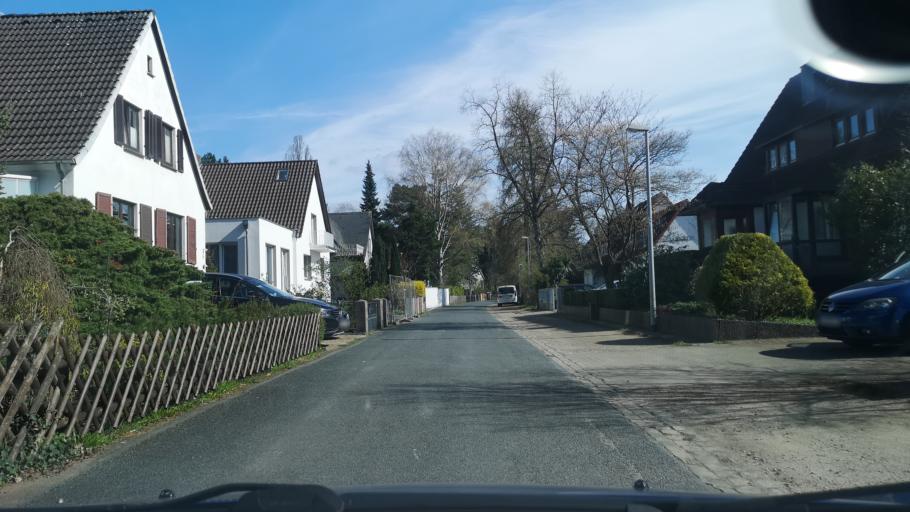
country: DE
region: Lower Saxony
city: Langenhagen
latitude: 52.4371
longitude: 9.7917
